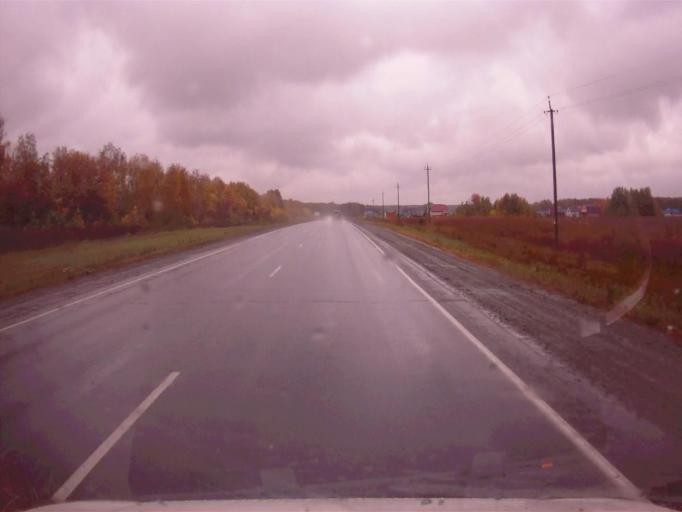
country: RU
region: Chelyabinsk
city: Argayash
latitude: 55.4054
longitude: 61.0611
